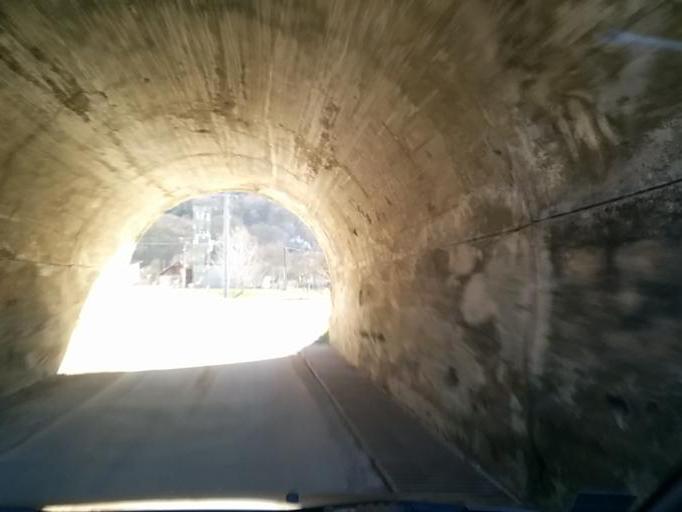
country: SK
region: Nitriansky
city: Cachtice
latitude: 48.7183
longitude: 17.7328
